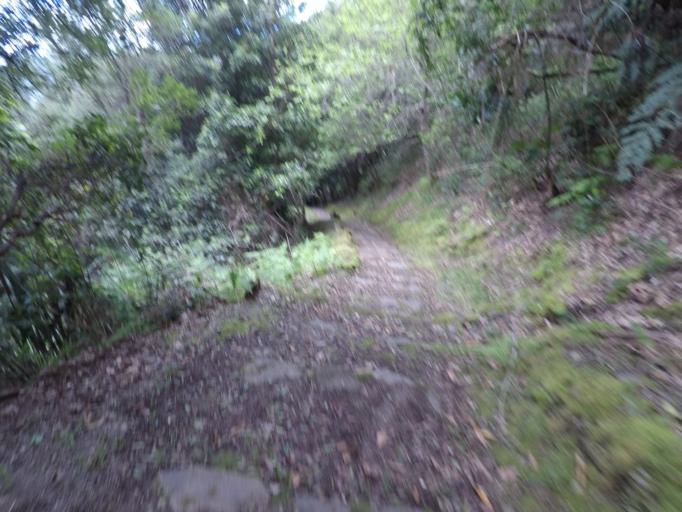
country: PT
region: Madeira
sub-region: Camara de Lobos
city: Curral das Freiras
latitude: 32.7783
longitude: -16.9798
